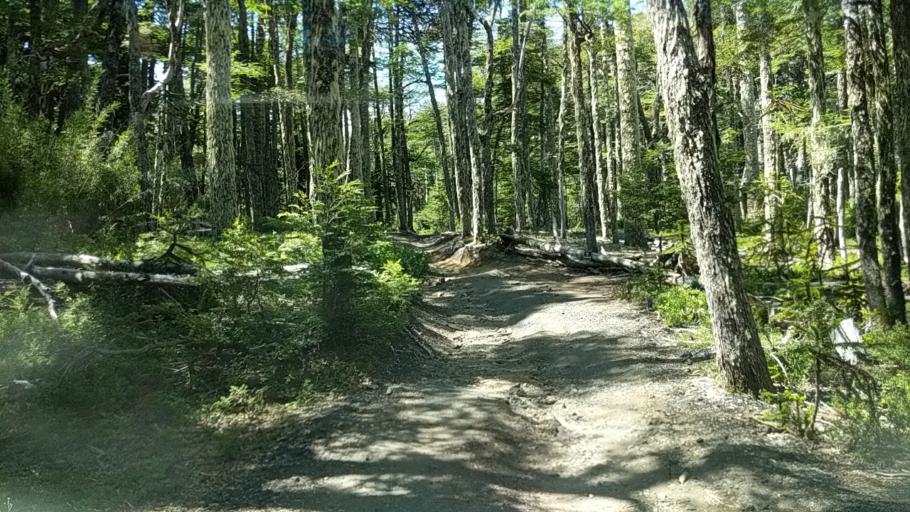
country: CL
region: Araucania
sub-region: Provincia de Cautin
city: Pucon
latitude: -39.4656
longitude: -71.8525
